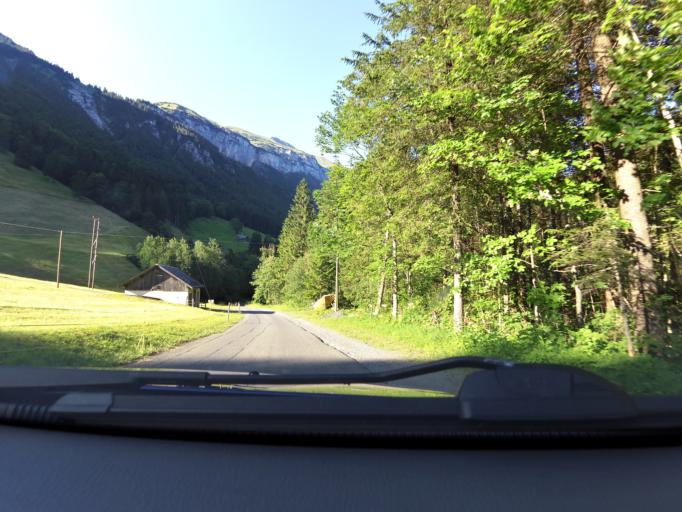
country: CH
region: Nidwalden
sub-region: Nidwalden
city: Emmetten
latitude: 46.9064
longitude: 8.5268
